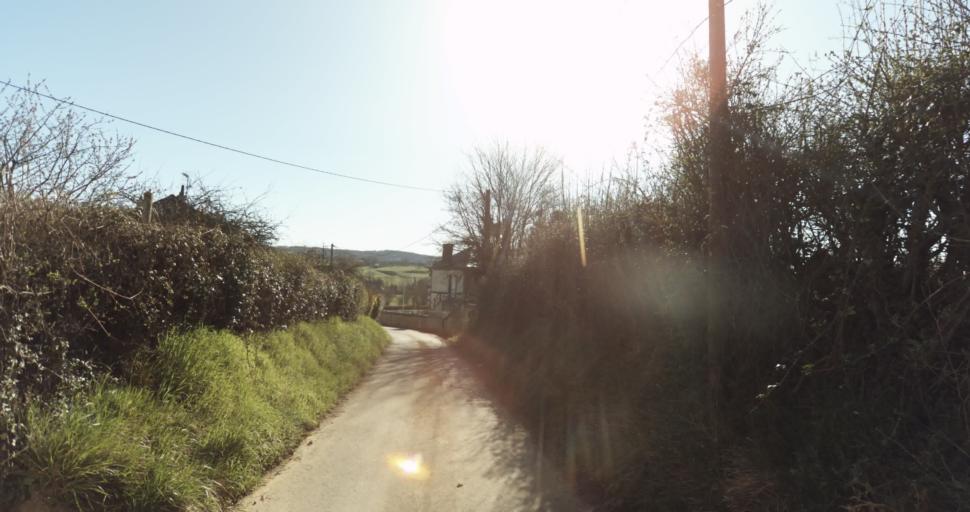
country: FR
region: Lower Normandy
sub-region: Departement du Calvados
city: Saint-Pierre-sur-Dives
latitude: 48.9771
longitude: 0.0353
